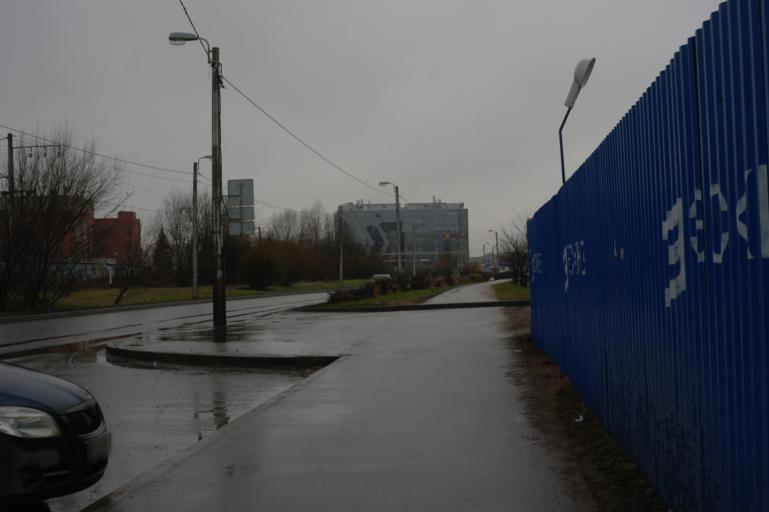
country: RU
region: Leningrad
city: Krestovskiy ostrov
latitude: 59.9886
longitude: 30.2616
